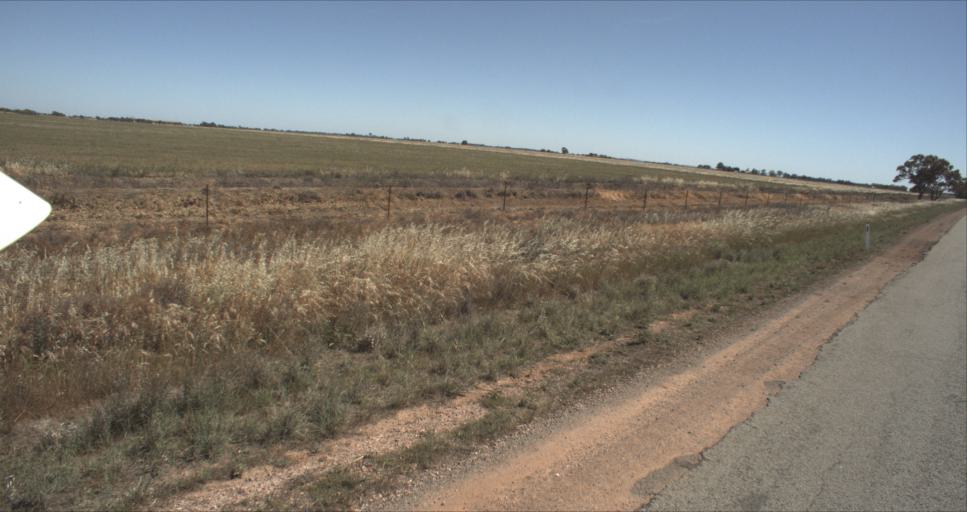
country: AU
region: New South Wales
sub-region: Leeton
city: Leeton
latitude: -34.5646
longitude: 146.3121
